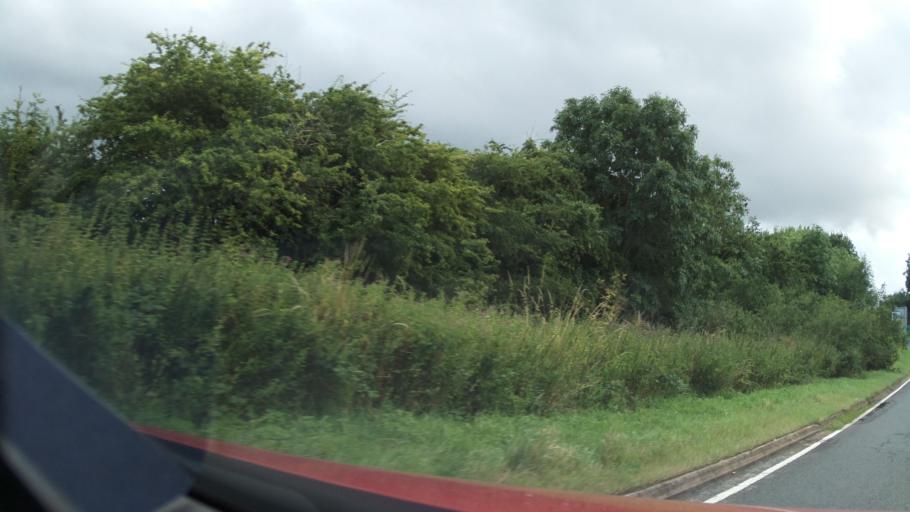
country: GB
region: England
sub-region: Warwickshire
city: Long Itchington
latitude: 52.2832
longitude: -1.3588
